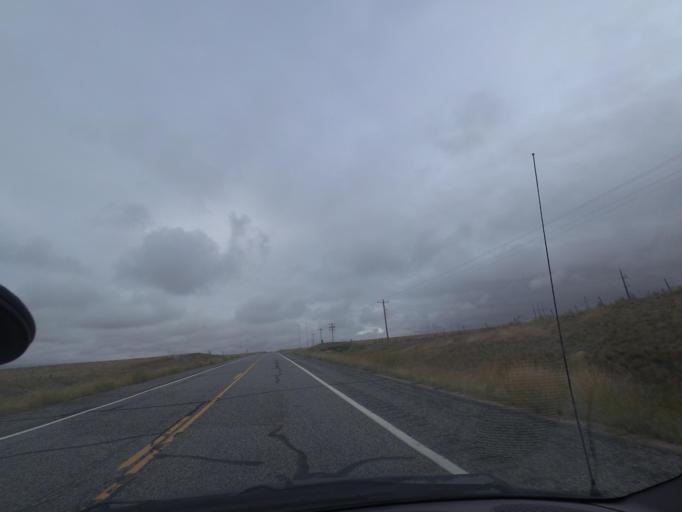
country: US
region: Colorado
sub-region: Washington County
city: Akron
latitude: 39.7393
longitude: -103.3987
